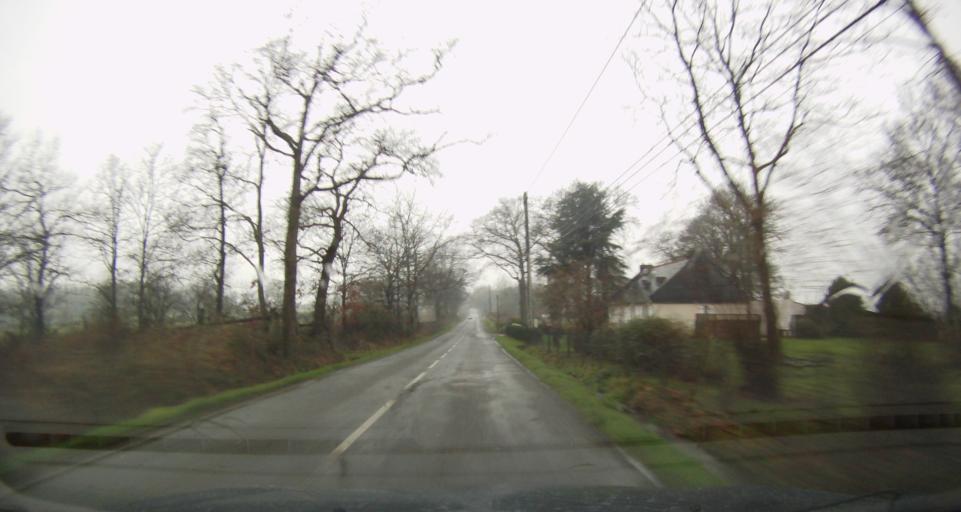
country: FR
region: Brittany
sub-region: Departement d'Ille-et-Vilaine
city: Orgeres
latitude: 47.9759
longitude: -1.6794
